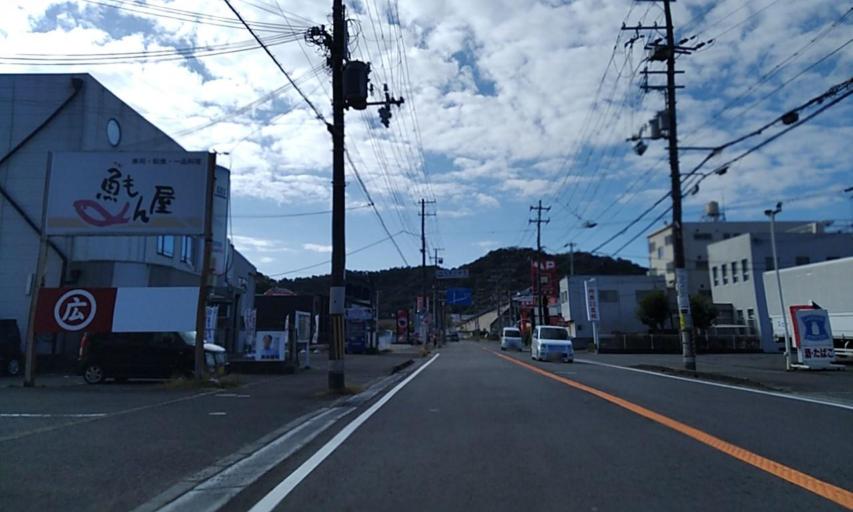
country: JP
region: Wakayama
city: Minato
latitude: 34.1974
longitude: 135.1589
